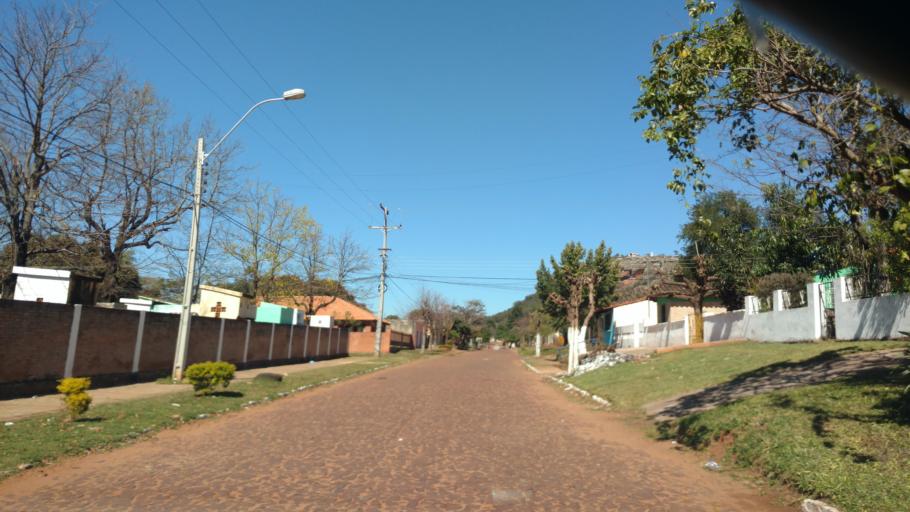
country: PY
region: Paraguari
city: Yaguaron
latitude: -25.5631
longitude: -57.2909
